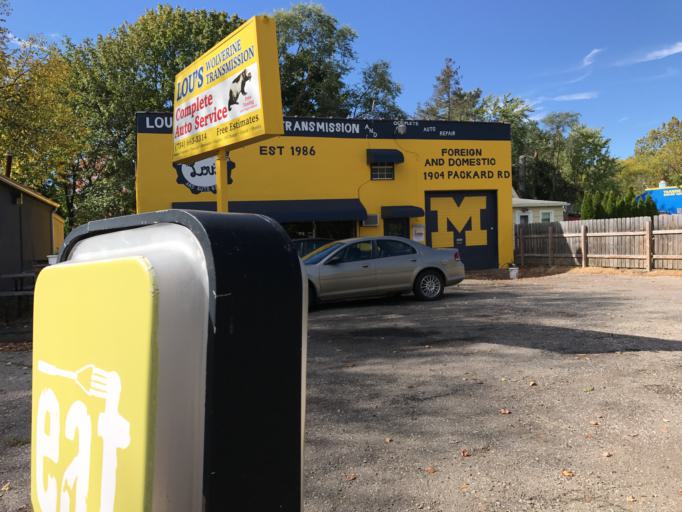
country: US
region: Michigan
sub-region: Washtenaw County
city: Ann Arbor
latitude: 42.2587
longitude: -83.7285
